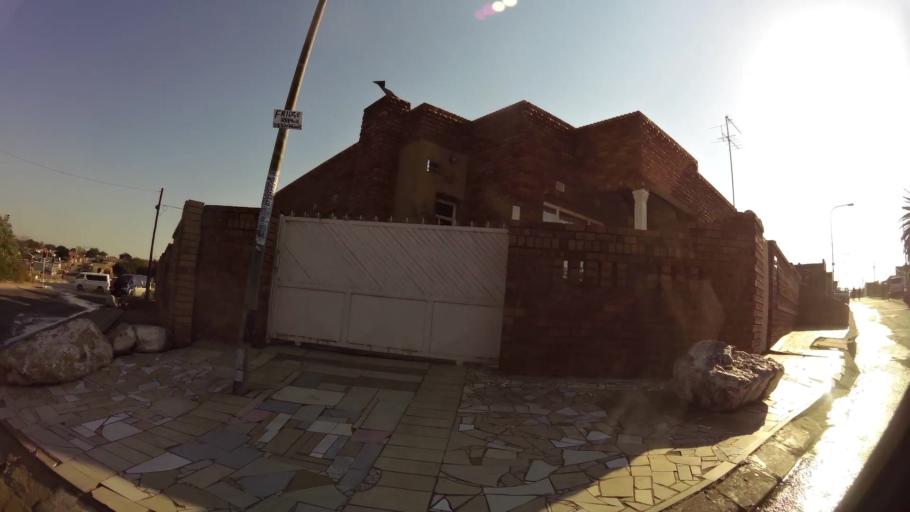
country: ZA
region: Gauteng
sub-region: City of Johannesburg Metropolitan Municipality
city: Soweto
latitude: -26.2540
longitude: 27.9458
